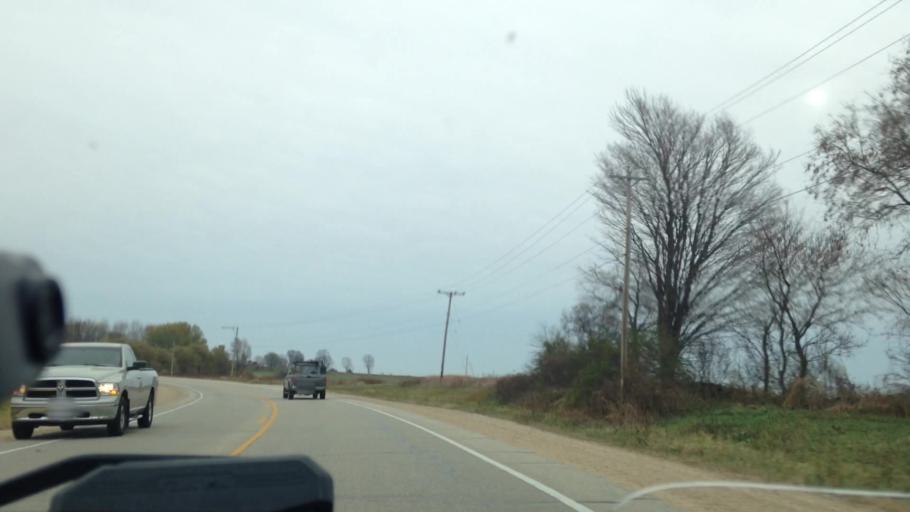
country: US
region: Wisconsin
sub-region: Dodge County
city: Theresa
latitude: 43.4215
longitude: -88.4093
